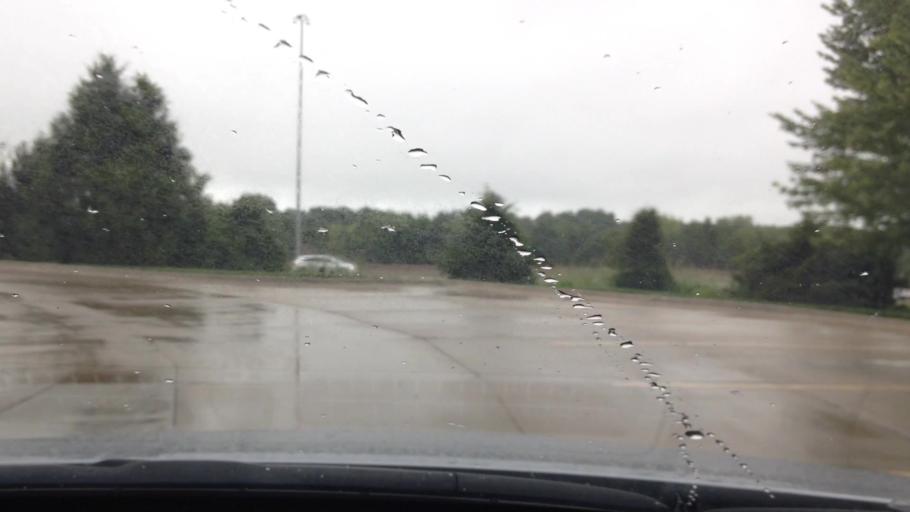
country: US
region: Kansas
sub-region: Wyandotte County
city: Bonner Springs
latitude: 39.0970
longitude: -94.8849
